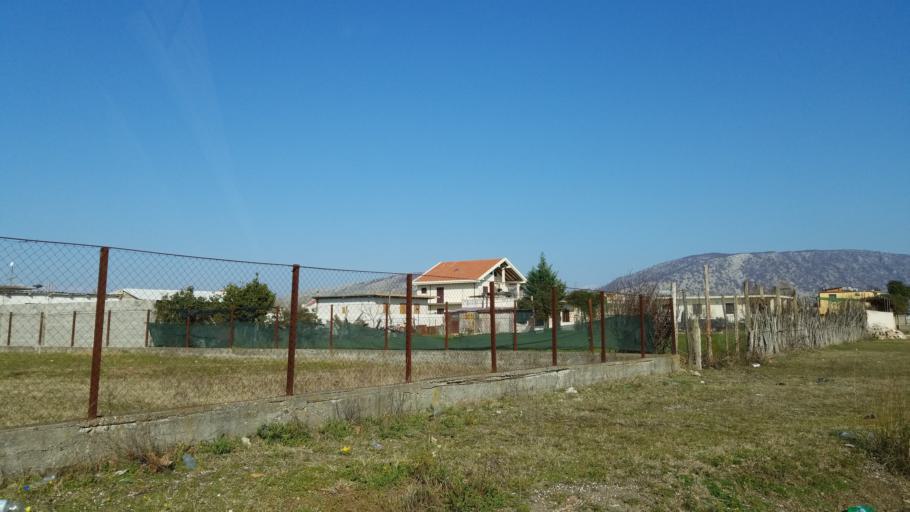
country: AL
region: Shkoder
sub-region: Rrethi i Shkodres
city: Velipoje
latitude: 41.8689
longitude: 19.4115
